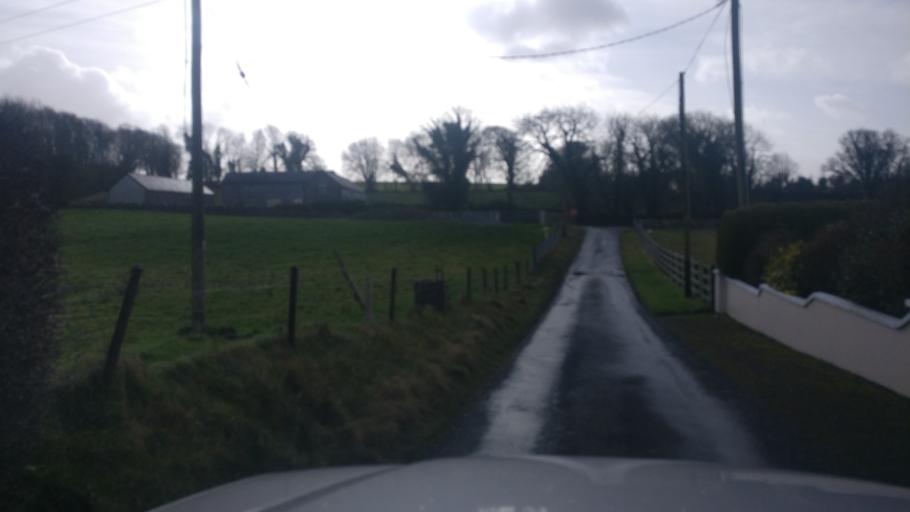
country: IE
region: Connaught
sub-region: County Galway
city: Loughrea
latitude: 53.2730
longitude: -8.5936
